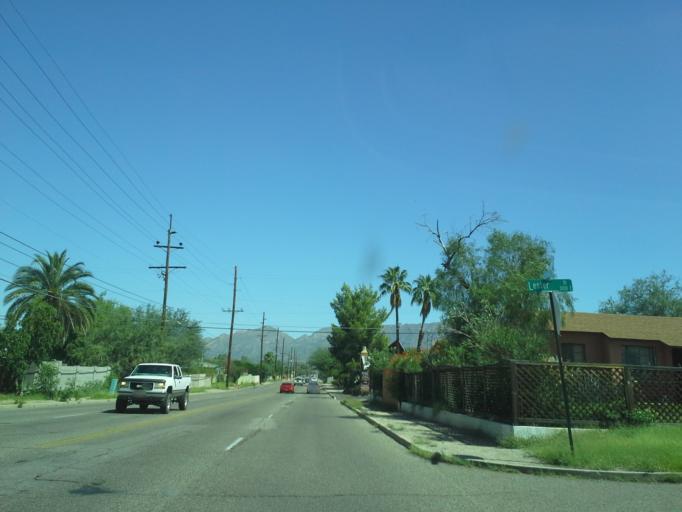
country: US
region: Arizona
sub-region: Pima County
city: Tucson
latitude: 32.2439
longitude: -110.9267
